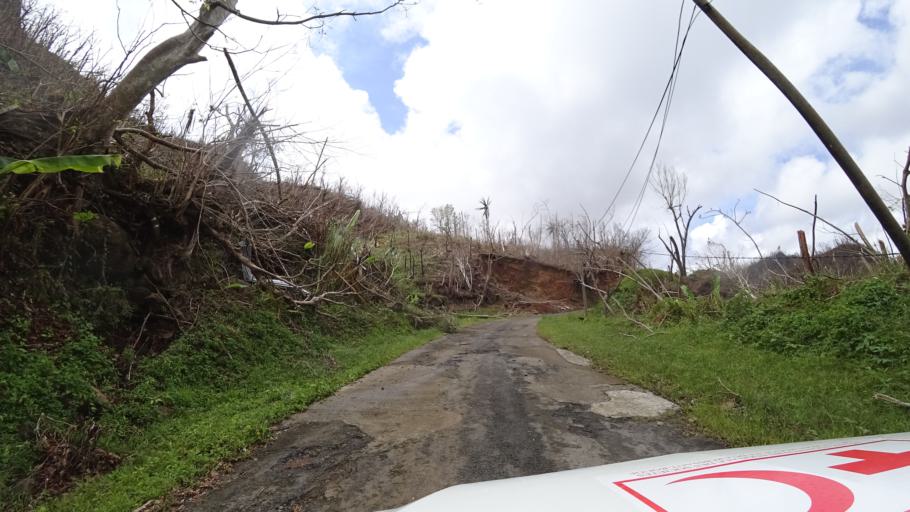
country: DM
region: Saint David
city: Rosalie
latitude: 15.3998
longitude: -61.2565
